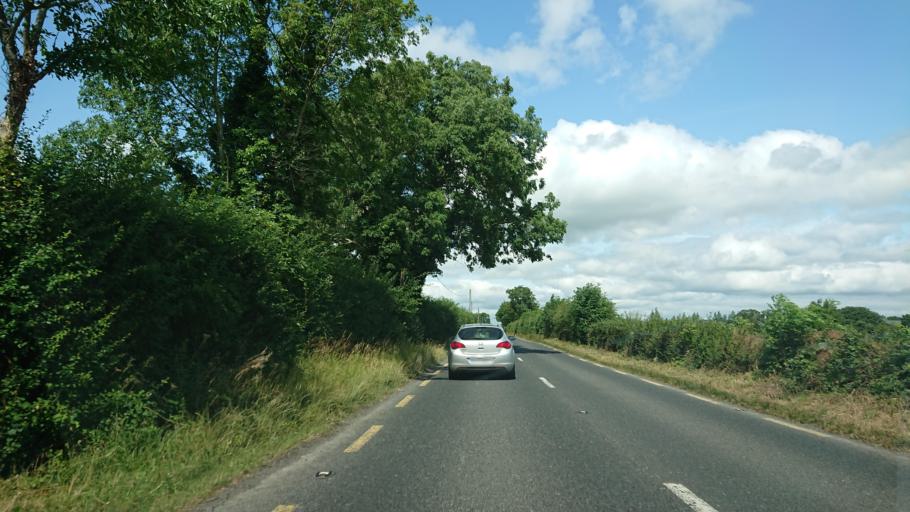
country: IE
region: Leinster
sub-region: Kildare
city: Kilcock
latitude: 53.3600
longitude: -6.6966
